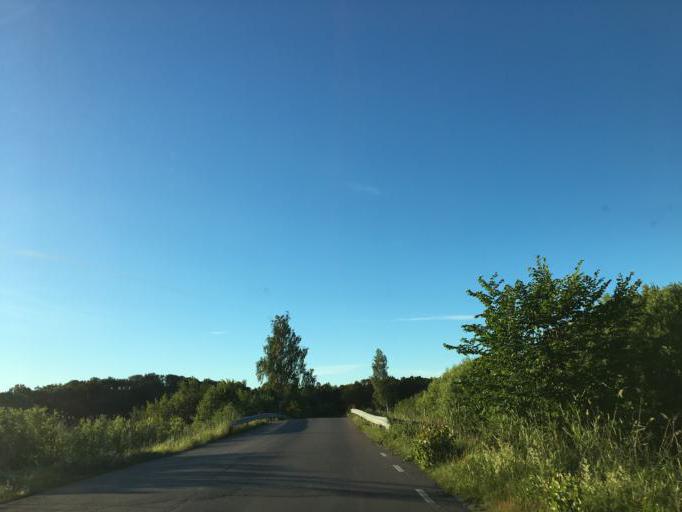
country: SE
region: Vaestmanland
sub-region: Vasteras
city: Vasteras
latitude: 59.5194
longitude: 16.5291
